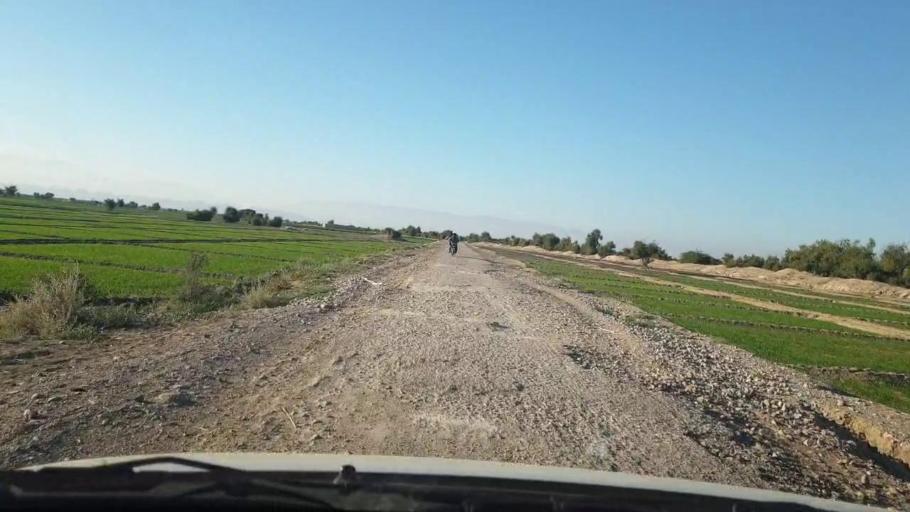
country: PK
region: Sindh
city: Johi
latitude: 26.7633
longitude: 67.4658
